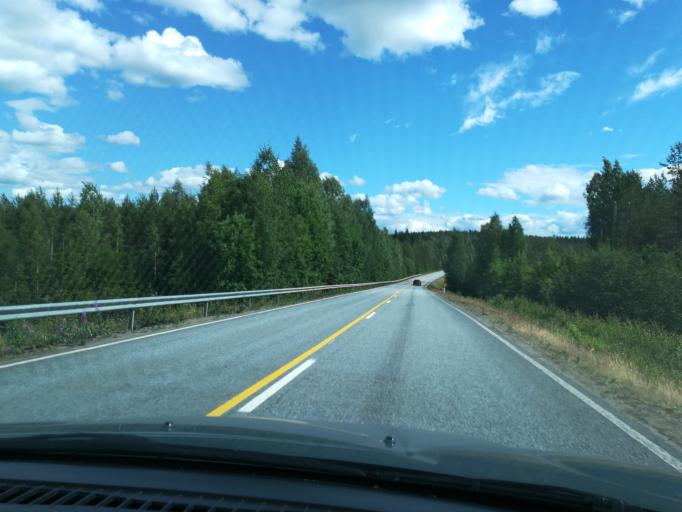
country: FI
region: Southern Savonia
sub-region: Mikkeli
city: Hirvensalmi
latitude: 61.6604
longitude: 26.9747
